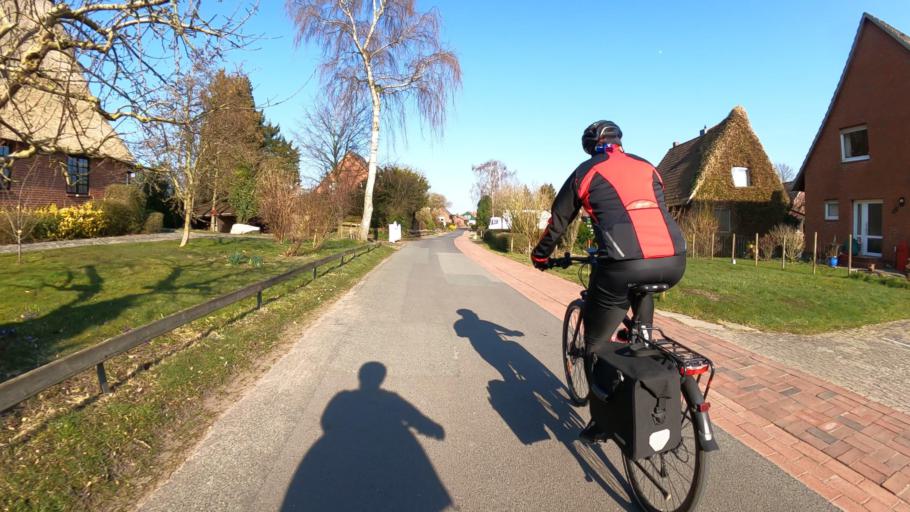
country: DE
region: Schleswig-Holstein
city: Seester
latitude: 53.7250
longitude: 9.5907
